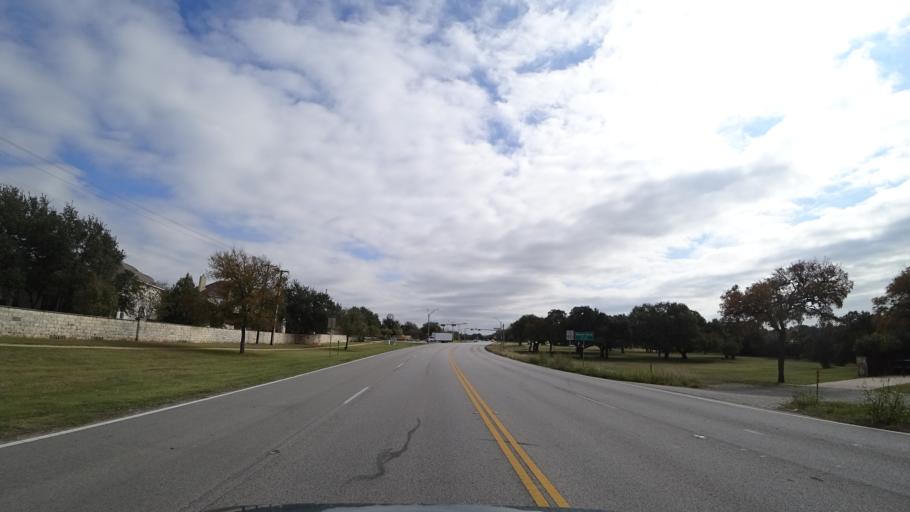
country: US
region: Texas
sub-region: Williamson County
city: Brushy Creek
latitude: 30.5314
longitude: -97.7244
